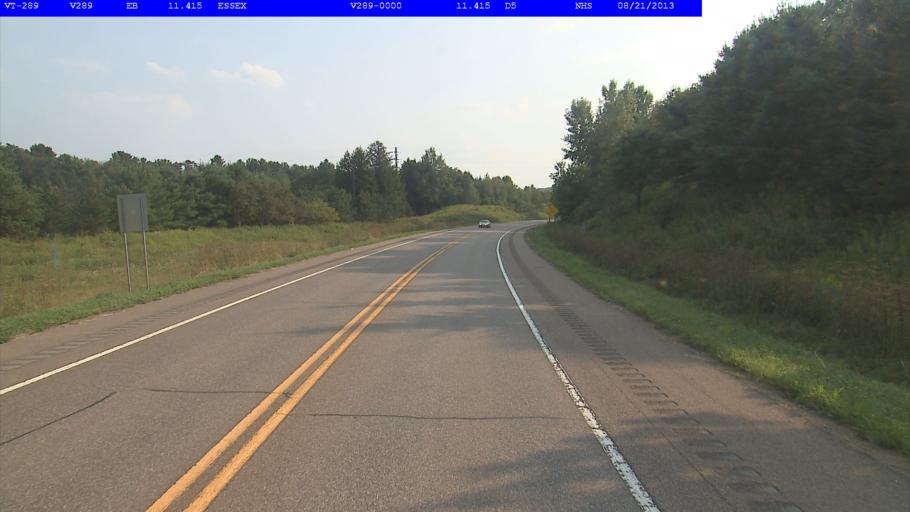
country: US
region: Vermont
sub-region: Chittenden County
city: Essex Junction
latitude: 44.4880
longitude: -73.0638
